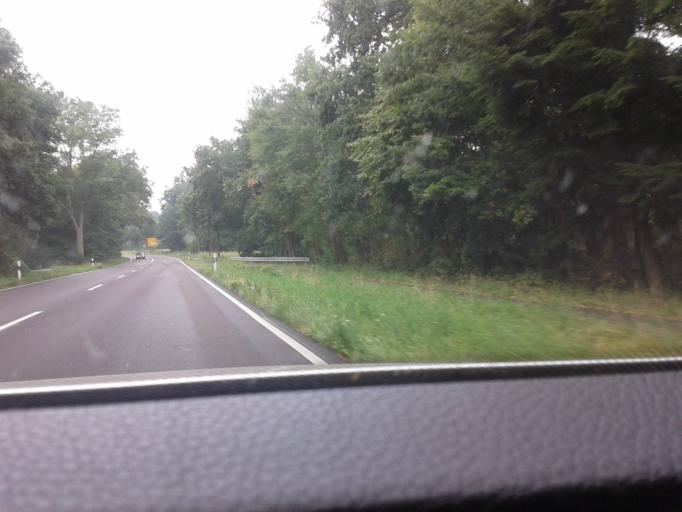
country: DE
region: Lower Saxony
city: Sassenburg
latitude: 52.4969
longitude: 10.6155
